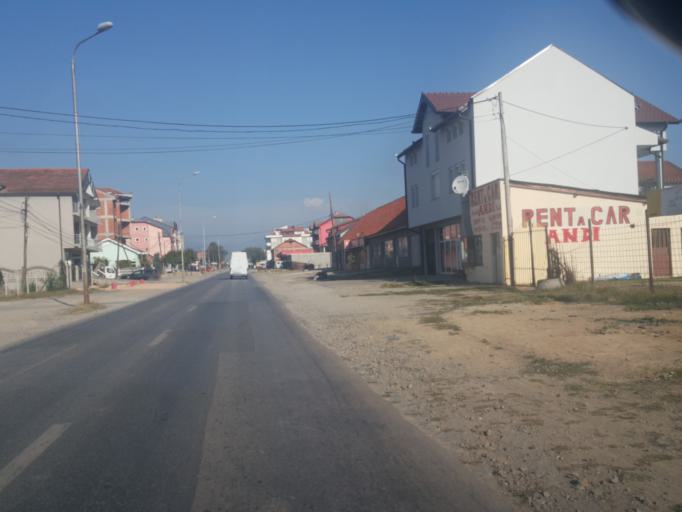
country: XK
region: Gjakova
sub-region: Komuna e Gjakoves
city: Gjakove
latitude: 42.4024
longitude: 20.4134
